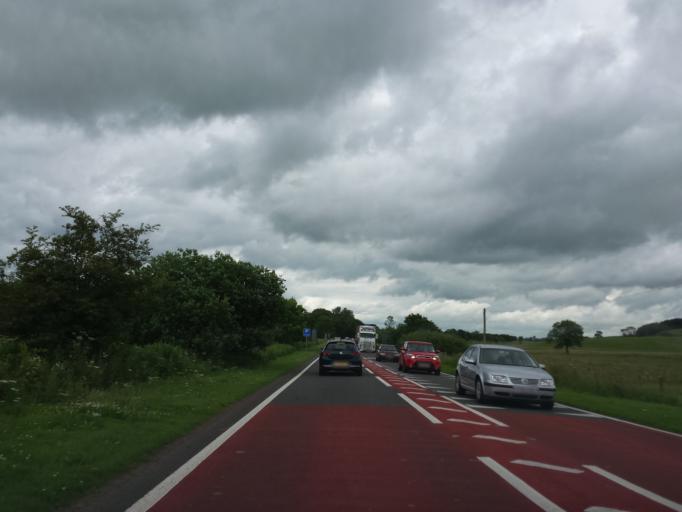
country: GB
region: Scotland
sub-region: Dumfries and Galloway
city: Dalbeattie
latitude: 55.0167
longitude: -3.8608
